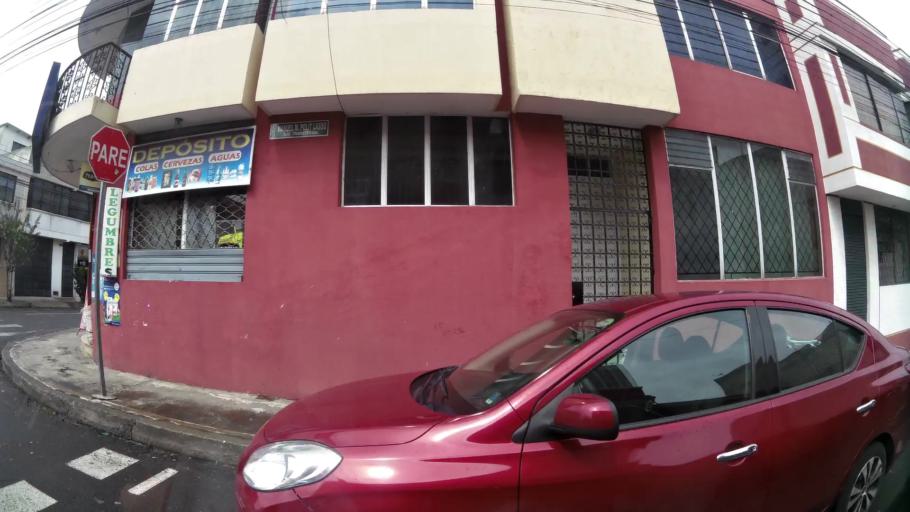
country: EC
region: Pichincha
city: Sangolqui
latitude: -0.2940
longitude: -78.4761
